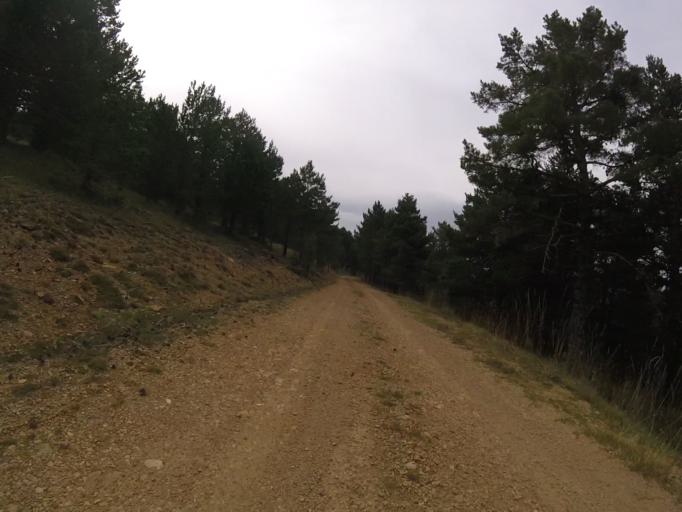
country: ES
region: Aragon
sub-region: Provincia de Teruel
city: Valdelinares
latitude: 40.3563
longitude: -0.5988
